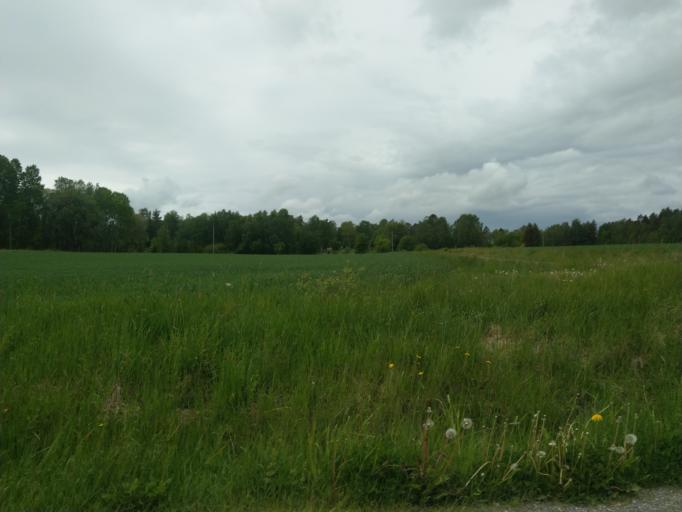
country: SE
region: Stockholm
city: Stenhamra
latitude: 59.4138
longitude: 17.6171
